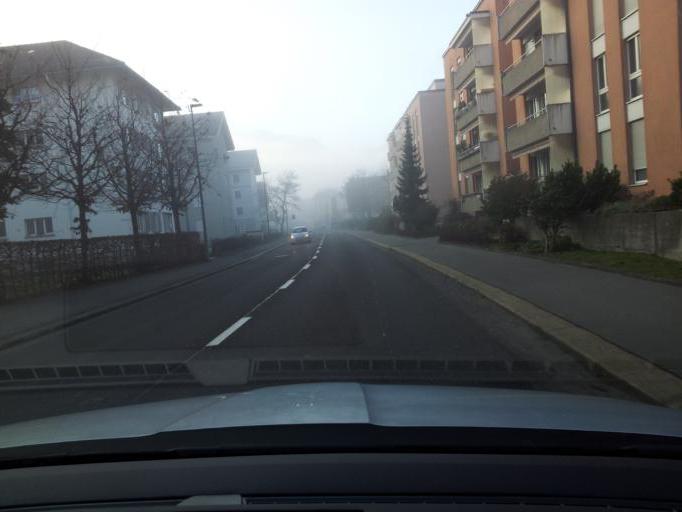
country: CH
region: Obwalden
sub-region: Obwalden
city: Sarnen
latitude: 46.9009
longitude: 8.2469
